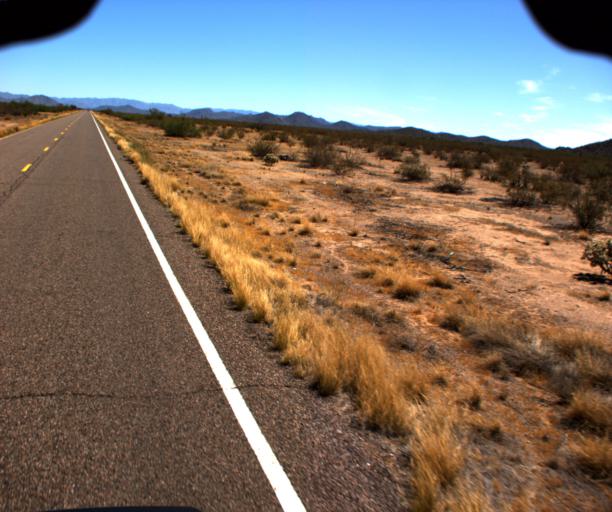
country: US
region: Arizona
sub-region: Yavapai County
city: Congress
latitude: 34.0162
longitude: -113.1015
